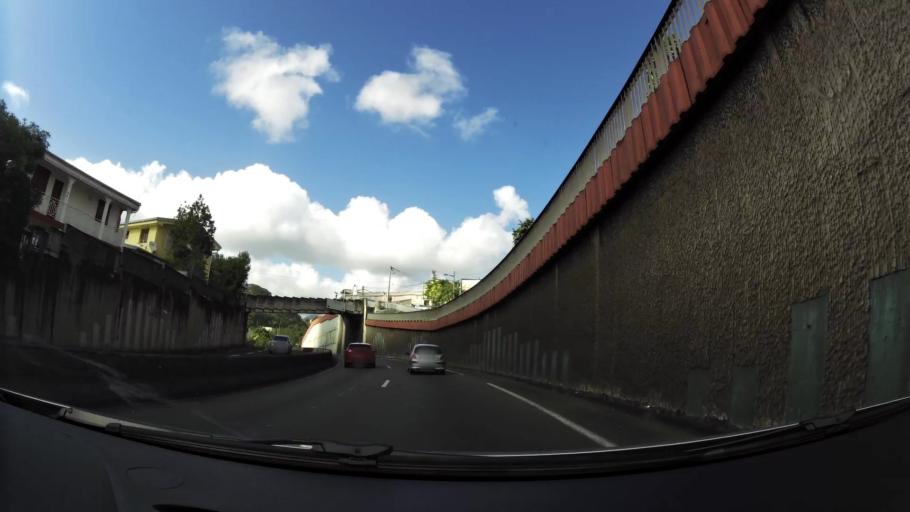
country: MQ
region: Martinique
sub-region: Martinique
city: Fort-de-France
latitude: 14.6141
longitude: -61.0702
